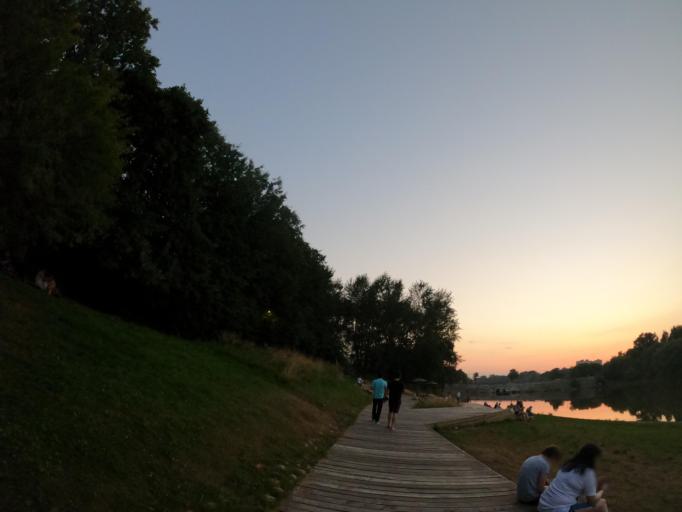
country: RU
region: Moscow
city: Lyublino
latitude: 55.6878
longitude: 37.7572
